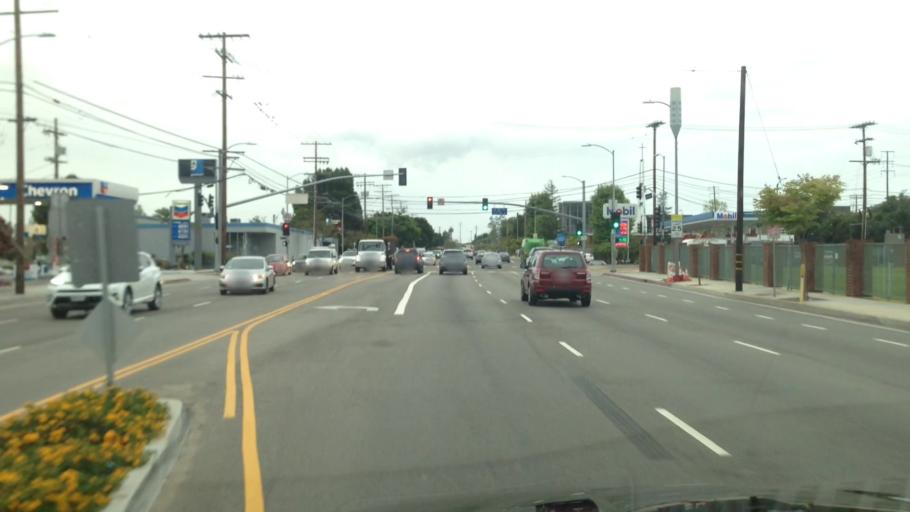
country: US
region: California
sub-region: Los Angeles County
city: Ladera Heights
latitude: 33.9725
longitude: -118.3948
